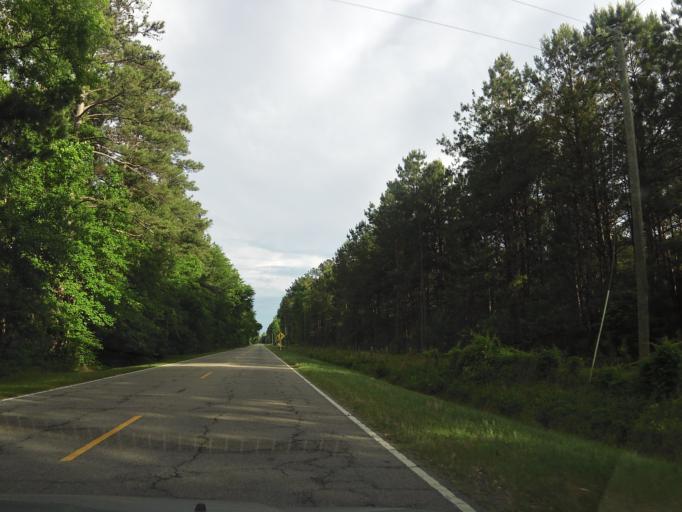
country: US
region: South Carolina
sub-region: Jasper County
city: Ridgeland
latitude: 32.5231
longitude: -81.1493
